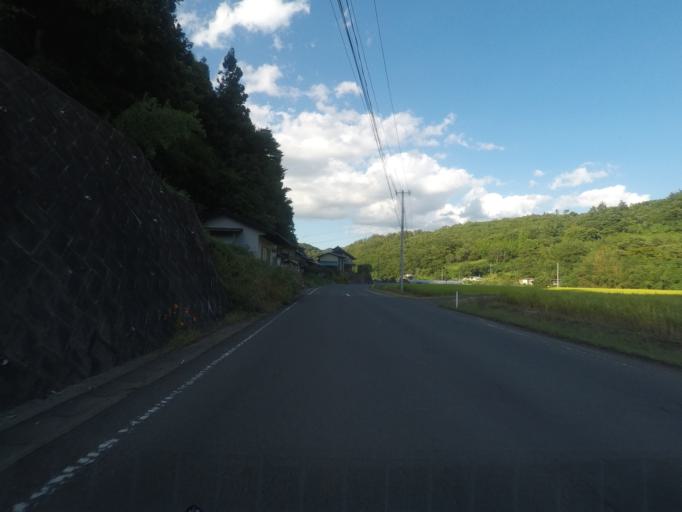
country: JP
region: Fukushima
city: Hobaramachi
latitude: 37.7525
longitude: 140.5592
